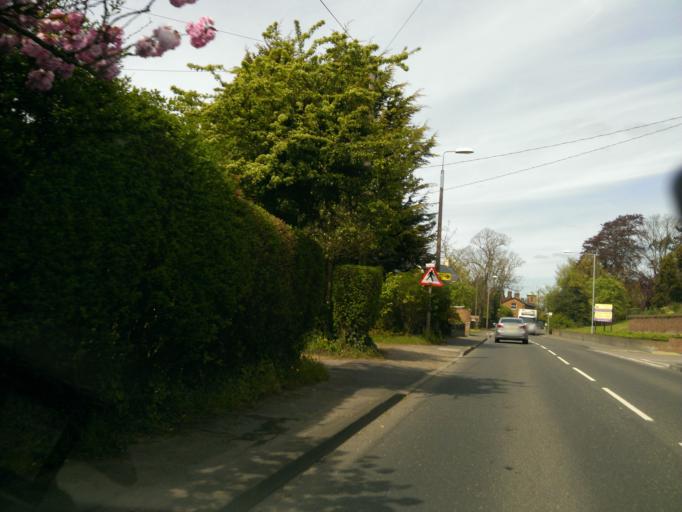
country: GB
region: England
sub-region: Essex
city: Earls Colne
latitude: 51.9425
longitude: 0.6486
